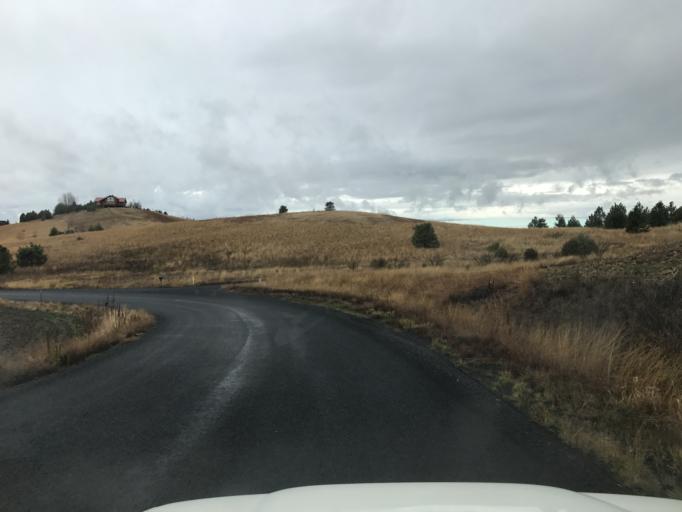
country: US
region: Idaho
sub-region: Latah County
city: Moscow
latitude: 46.7835
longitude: -116.9638
